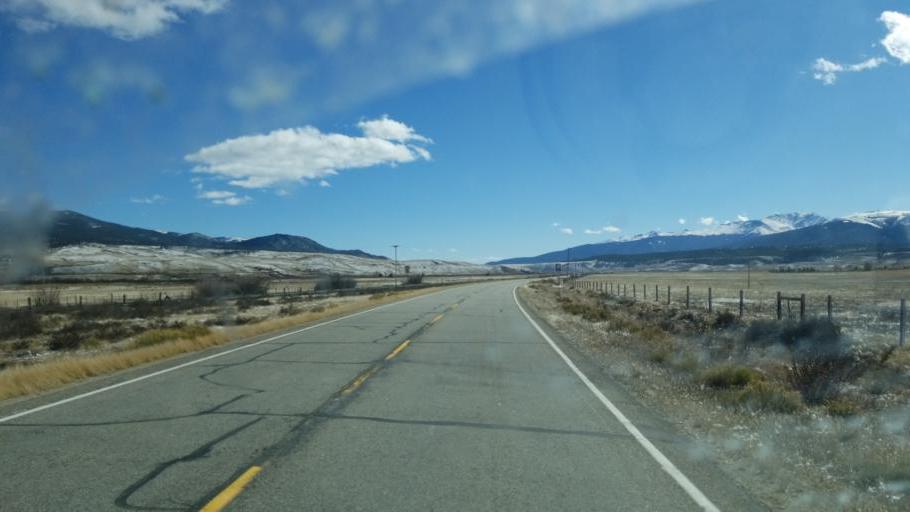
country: US
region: Colorado
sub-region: Lake County
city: Leadville
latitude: 39.1589
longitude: -106.3239
